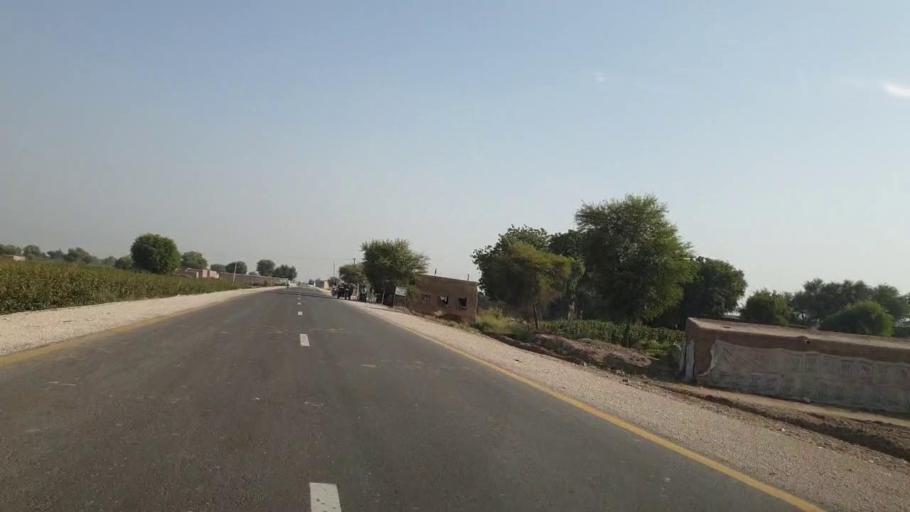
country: PK
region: Sindh
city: Sehwan
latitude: 26.4576
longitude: 67.8058
